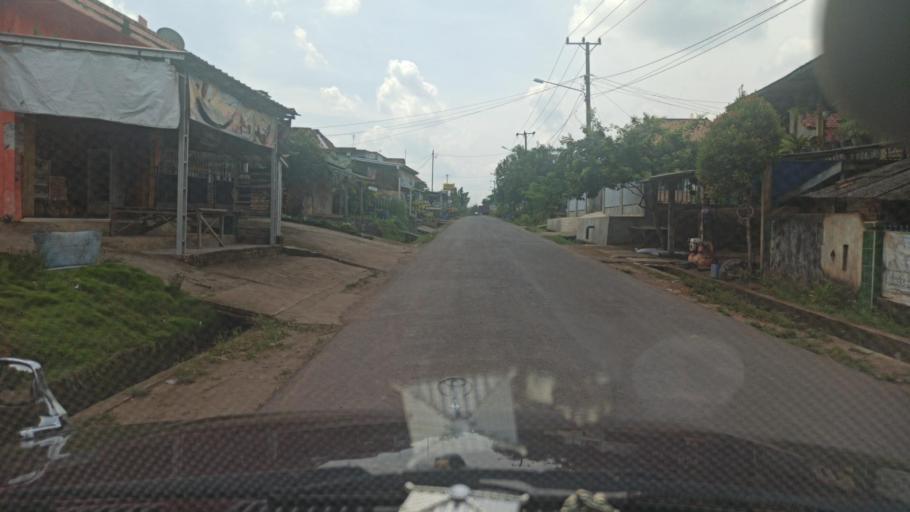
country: ID
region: South Sumatra
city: Gunungmenang
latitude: -3.3110
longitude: 104.1108
